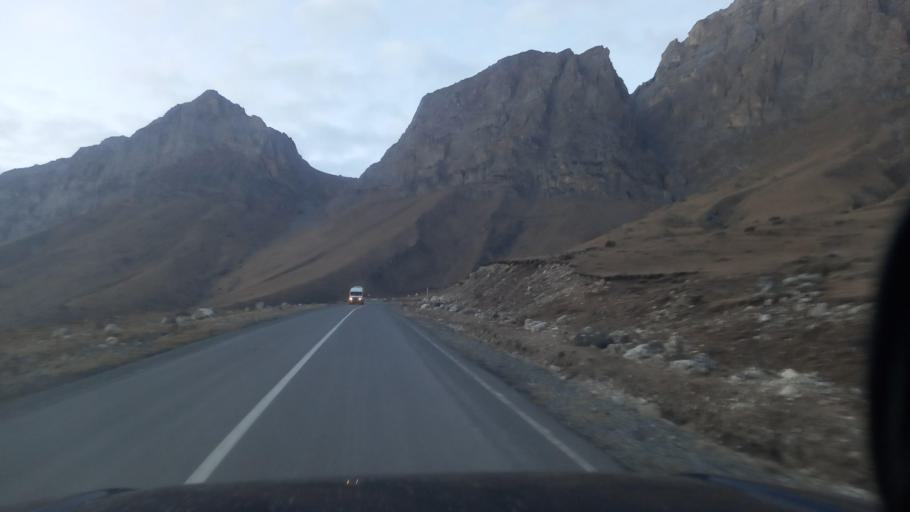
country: RU
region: Ingushetiya
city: Dzhayrakh
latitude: 42.8225
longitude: 44.8258
